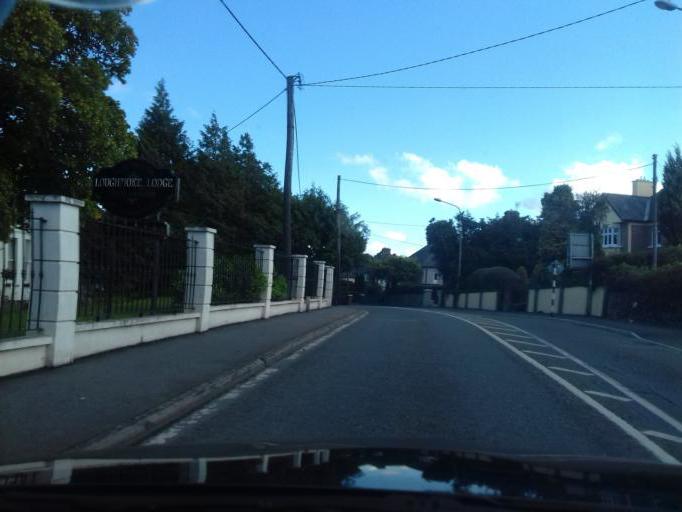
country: IE
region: Leinster
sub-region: Uibh Fhaili
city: Tullamore
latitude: 53.2691
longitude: -7.4900
